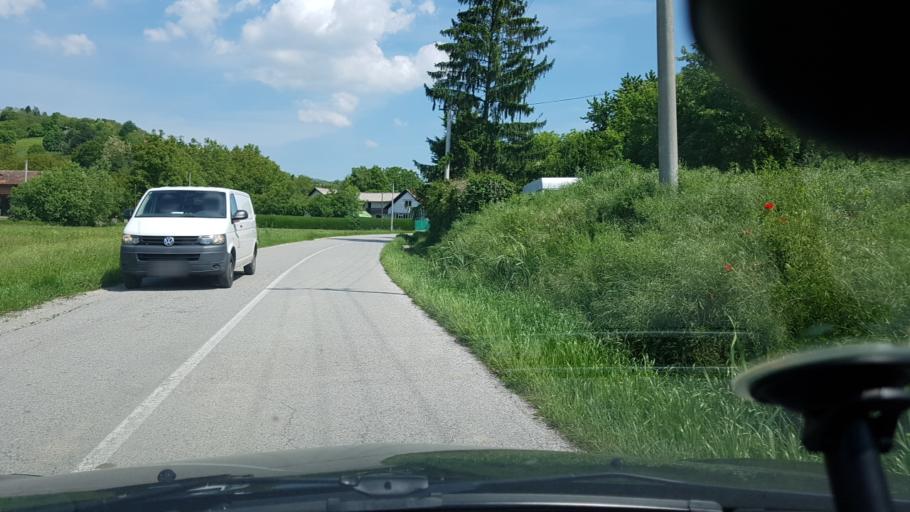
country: HR
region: Krapinsko-Zagorska
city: Marija Bistrica
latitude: 45.9359
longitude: 16.2000
